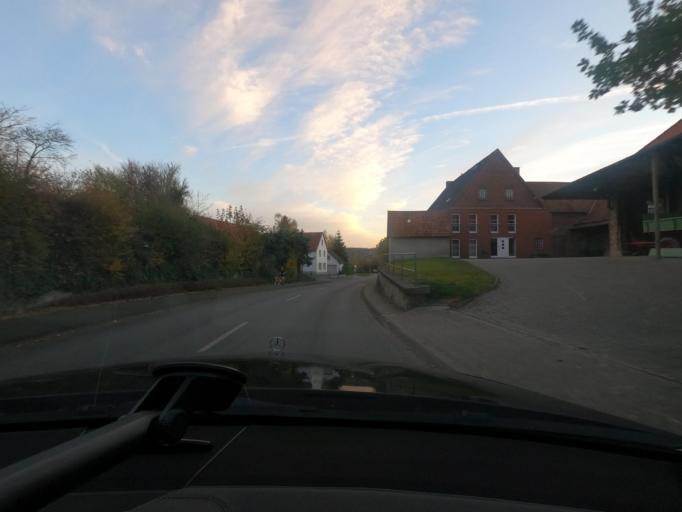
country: DE
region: North Rhine-Westphalia
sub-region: Regierungsbezirk Arnsberg
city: Mohnesee
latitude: 51.4949
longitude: 8.1312
